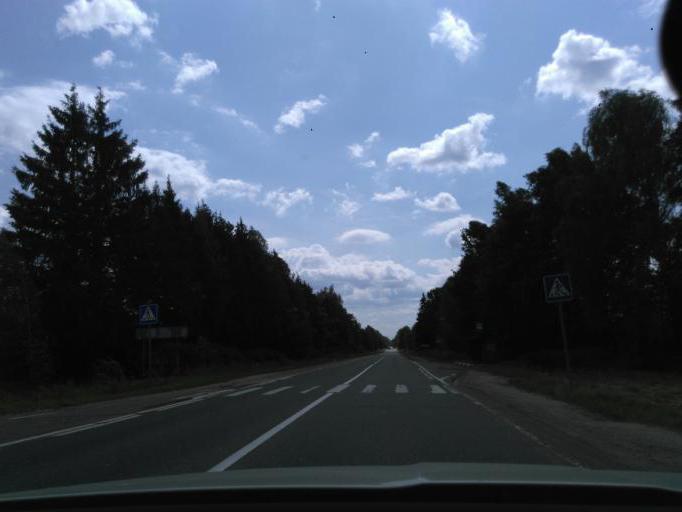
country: RU
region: Moskovskaya
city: Solnechnogorsk
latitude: 56.1367
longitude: 36.9195
